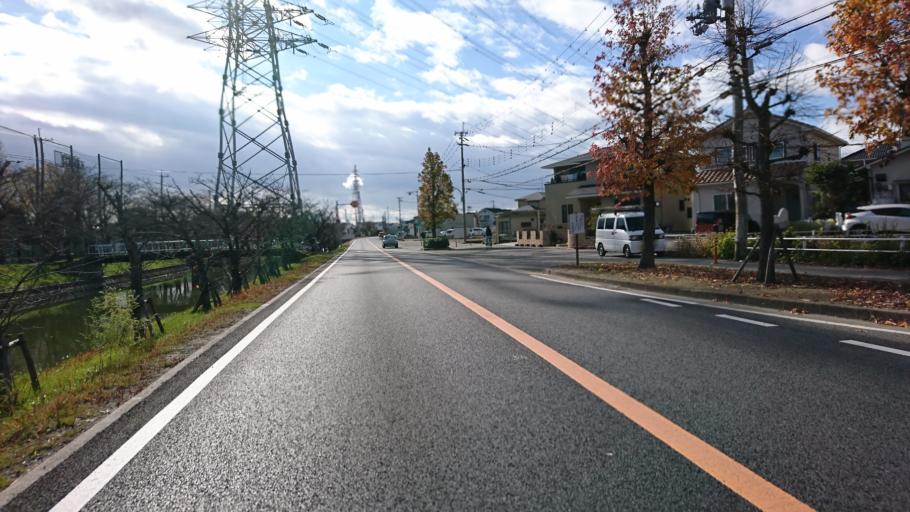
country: JP
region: Hyogo
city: Kakogawacho-honmachi
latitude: 34.7716
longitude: 134.7763
